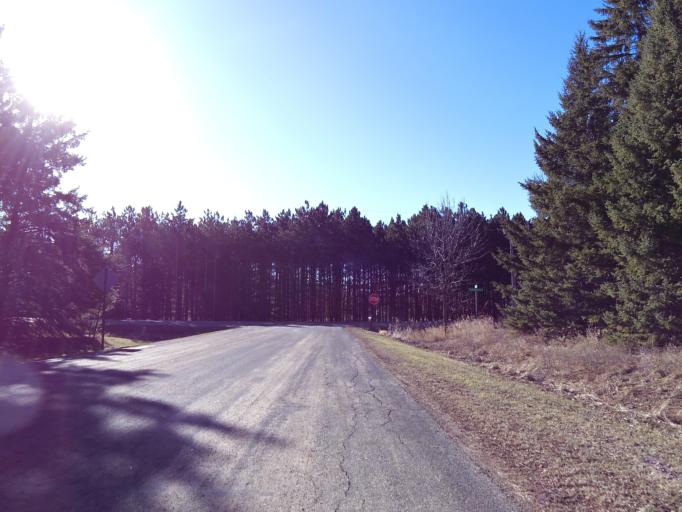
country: US
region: Minnesota
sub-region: Washington County
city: Bayport
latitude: 44.9830
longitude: -92.8218
